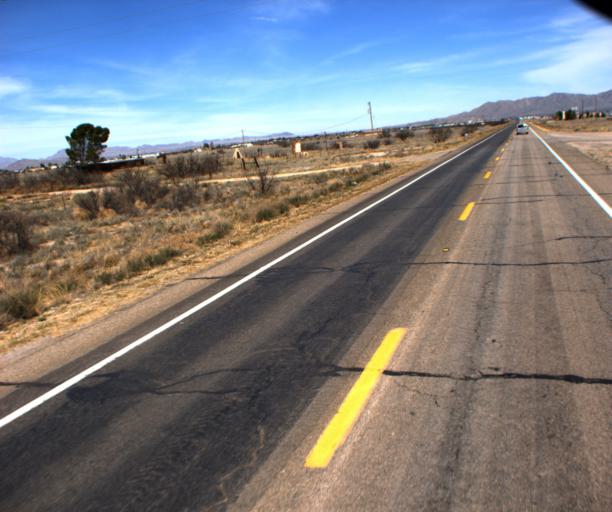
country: US
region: Arizona
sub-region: Cochise County
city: Willcox
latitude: 32.2279
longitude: -109.8633
